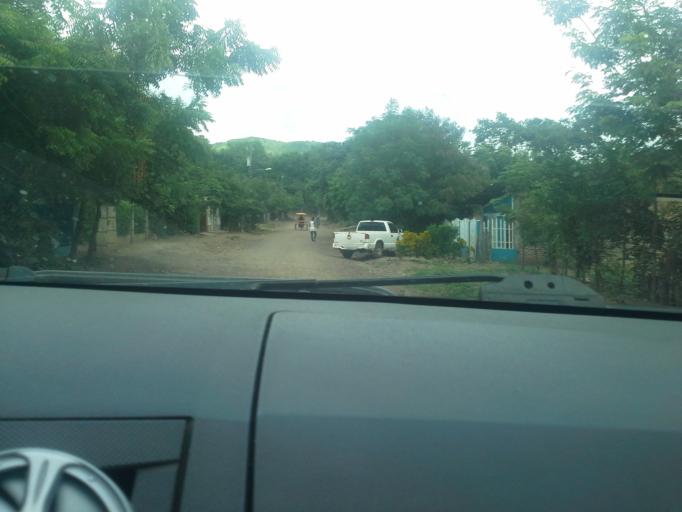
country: NI
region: Matagalpa
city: Ciudad Dario
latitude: 12.8552
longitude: -86.0918
